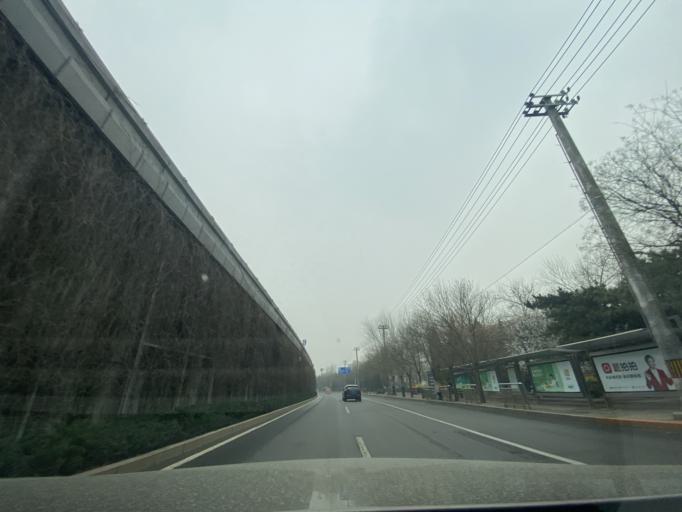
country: CN
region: Beijing
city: Sijiqing
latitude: 39.9671
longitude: 116.2685
